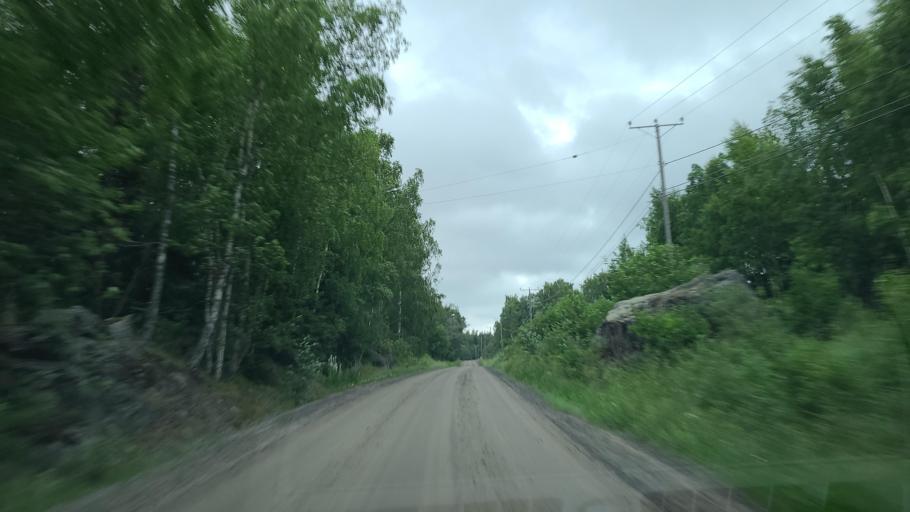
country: FI
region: Ostrobothnia
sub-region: Vaasa
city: Replot
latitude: 63.3103
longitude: 21.1581
